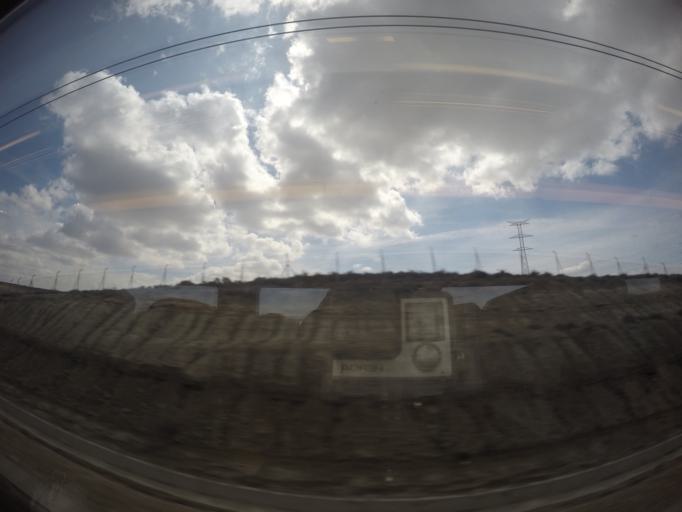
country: ES
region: Aragon
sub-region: Provincia de Huesca
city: Penalba
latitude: 41.5277
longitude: -0.0770
